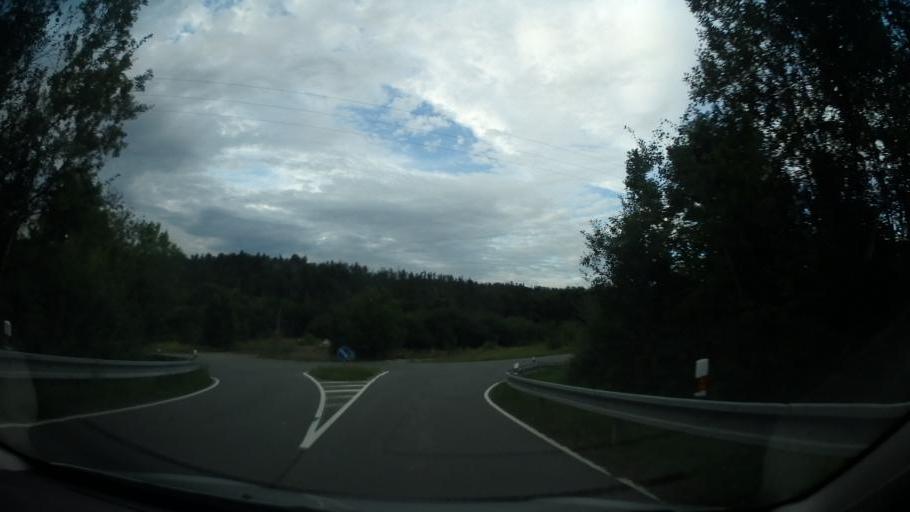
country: CZ
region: Olomoucky
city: Bila Lhota
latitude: 49.7026
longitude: 17.0016
